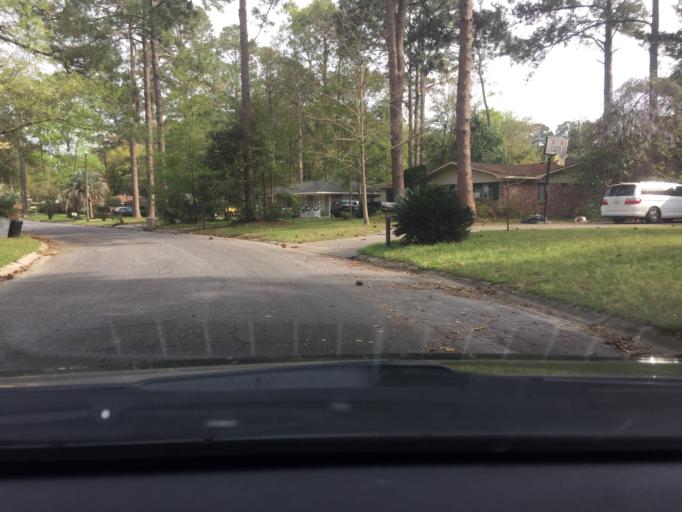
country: US
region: Georgia
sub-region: Chatham County
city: Montgomery
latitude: 31.9807
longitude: -81.1122
